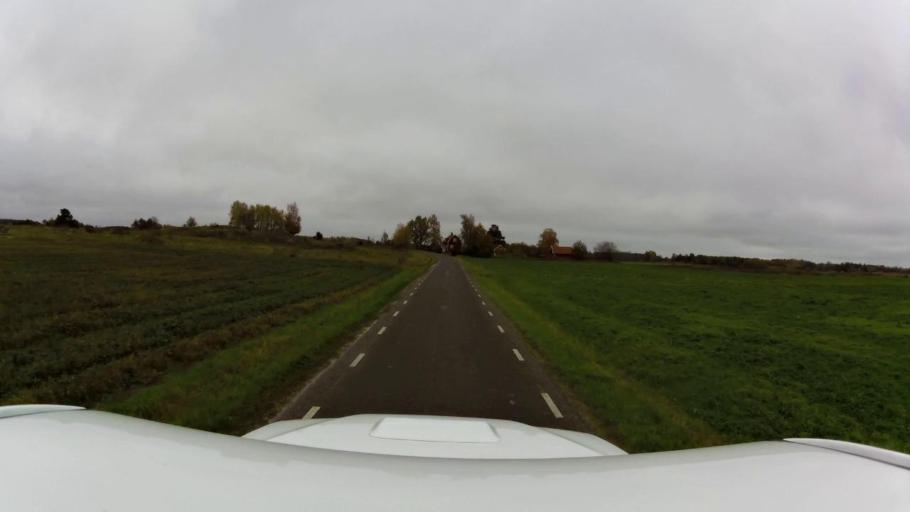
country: SE
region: OEstergoetland
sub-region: Linkopings Kommun
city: Linghem
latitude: 58.4813
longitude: 15.7906
